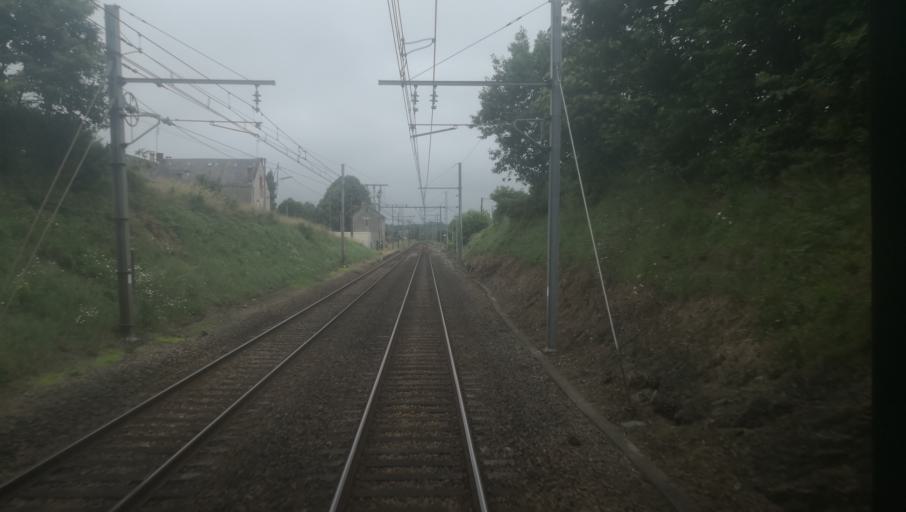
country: FR
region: Limousin
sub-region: Departement de la Creuse
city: Saint-Agnant-de-Versillat
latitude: 46.3238
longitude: 1.5284
